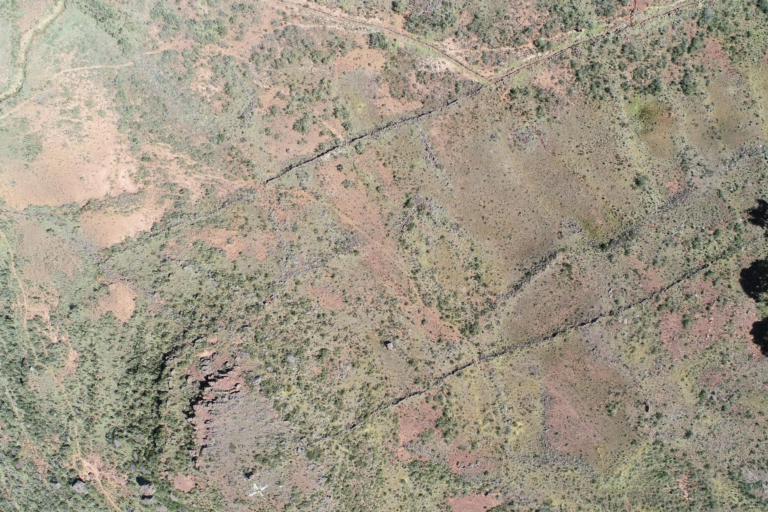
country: BO
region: La Paz
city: Tiahuanaco
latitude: -16.6056
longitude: -68.7754
